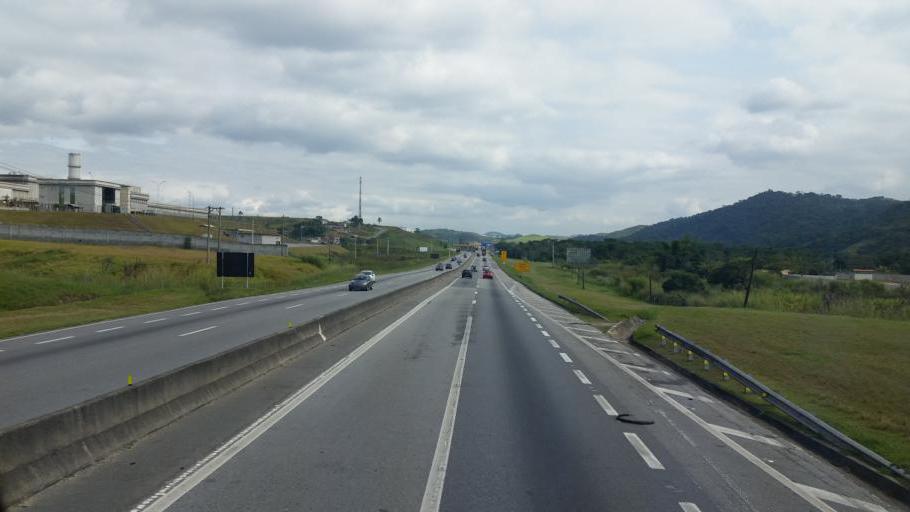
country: BR
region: Sao Paulo
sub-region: Santa Isabel
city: Santa Isabel
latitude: -23.3343
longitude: -46.1414
